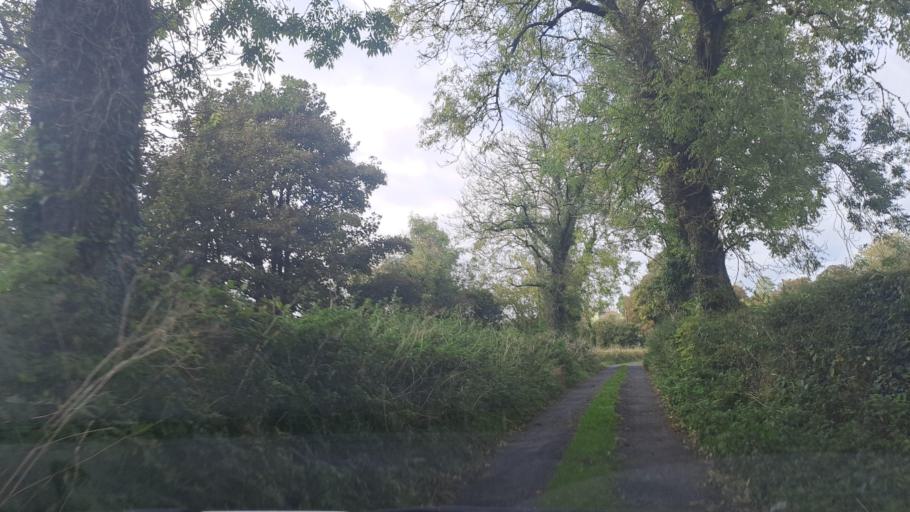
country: IE
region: Ulster
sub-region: An Cabhan
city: Kingscourt
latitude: 53.9995
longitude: -6.8154
